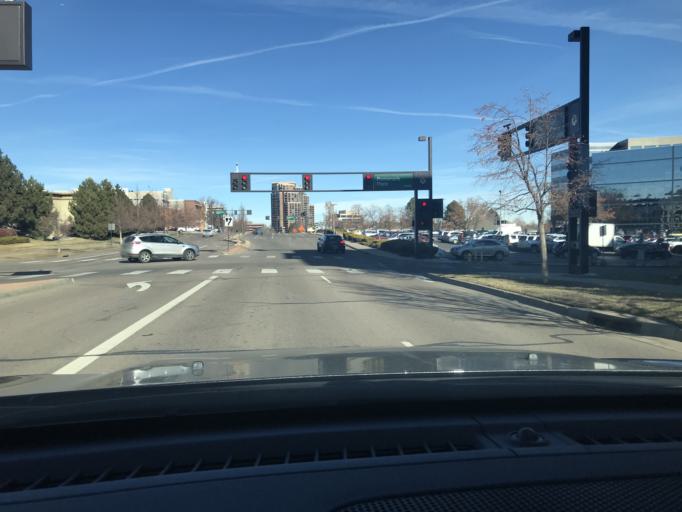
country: US
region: Colorado
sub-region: Arapahoe County
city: Castlewood
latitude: 39.6223
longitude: -104.8947
